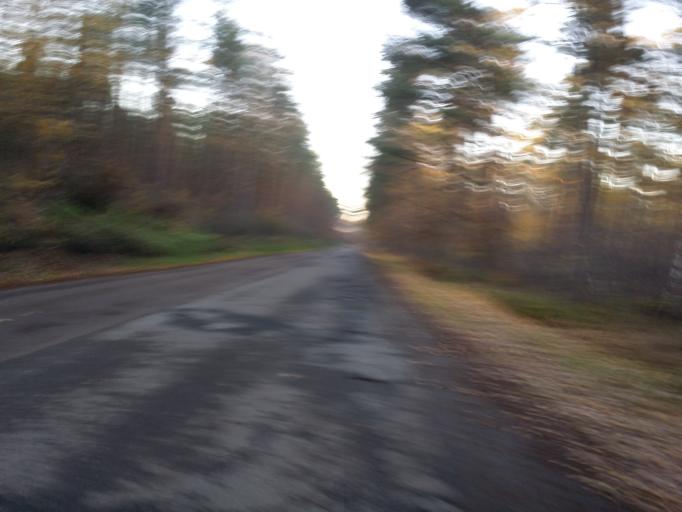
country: DE
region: Lower Saxony
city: Ahausen
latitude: 53.0790
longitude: 9.3057
